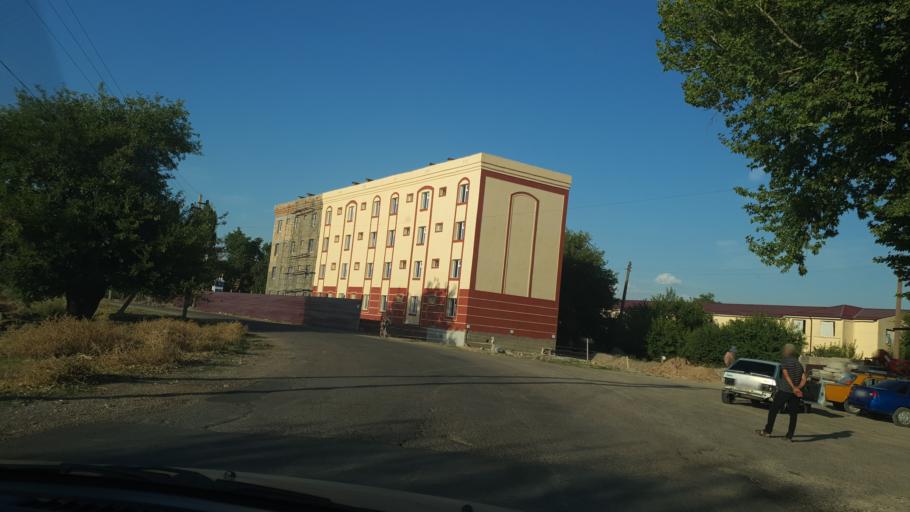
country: UZ
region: Toshkent
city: Tuytepa
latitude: 41.0868
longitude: 69.3531
